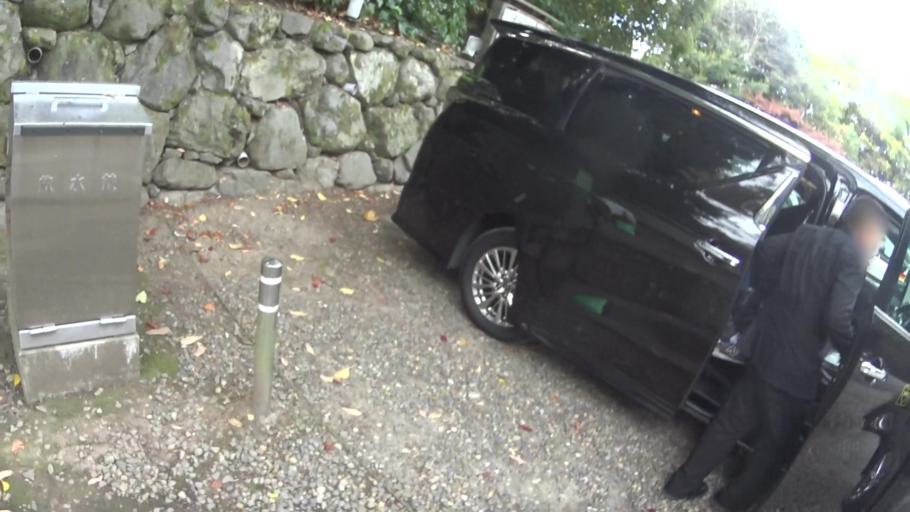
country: JP
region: Kyoto
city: Kyoto
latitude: 34.9773
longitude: 135.7790
